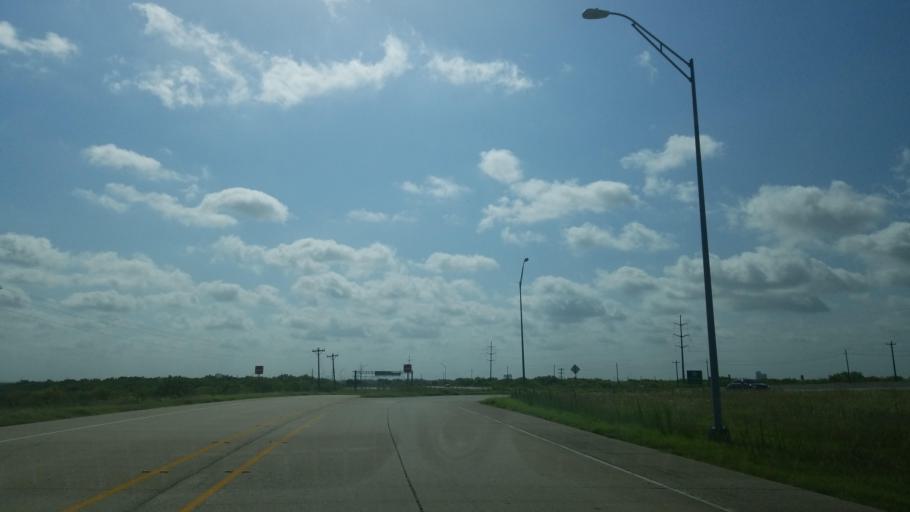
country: US
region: Texas
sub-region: Denton County
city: Denton
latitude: 33.2562
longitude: -97.1757
